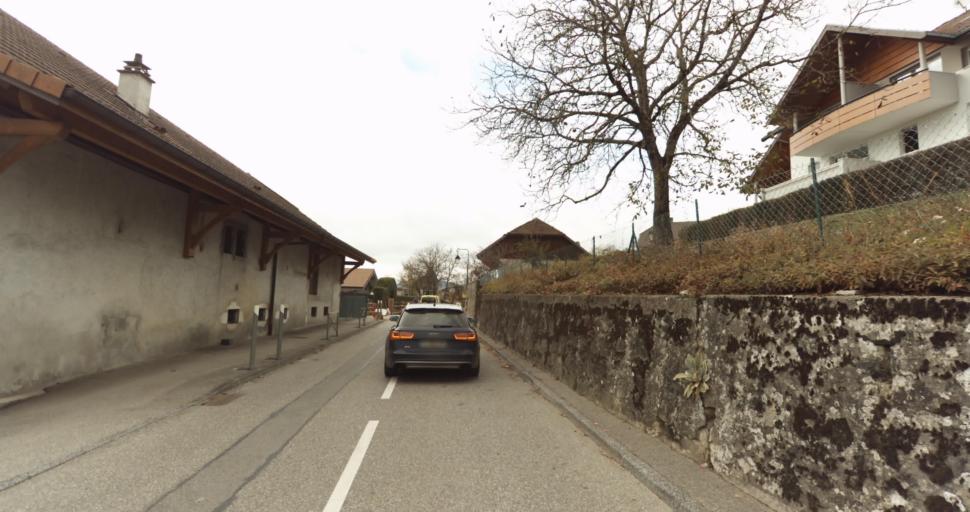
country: FR
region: Rhone-Alpes
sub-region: Departement de la Haute-Savoie
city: Pringy
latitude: 45.9446
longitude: 6.1449
